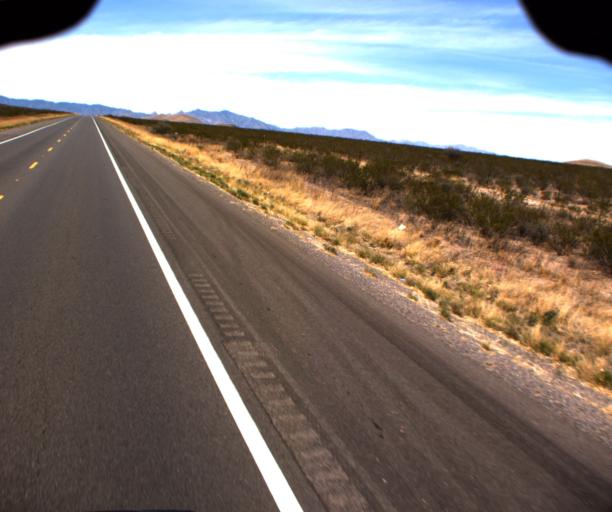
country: US
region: Arizona
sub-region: Cochise County
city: Willcox
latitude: 31.9056
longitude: -109.7329
